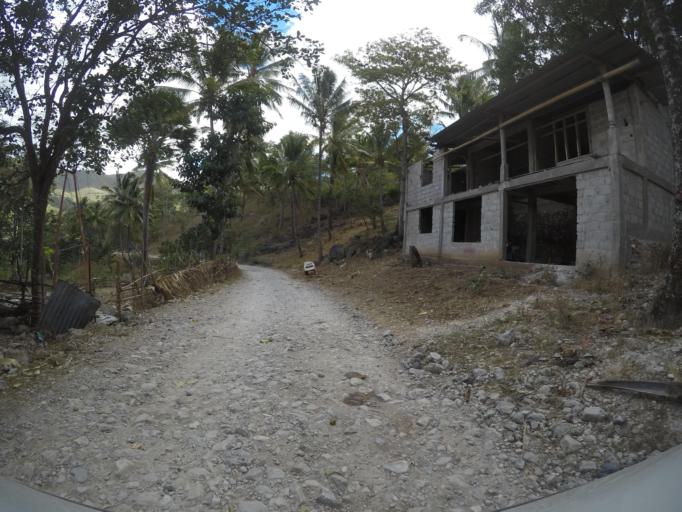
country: TL
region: Baucau
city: Baucau
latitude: -8.5237
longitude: 126.6944
